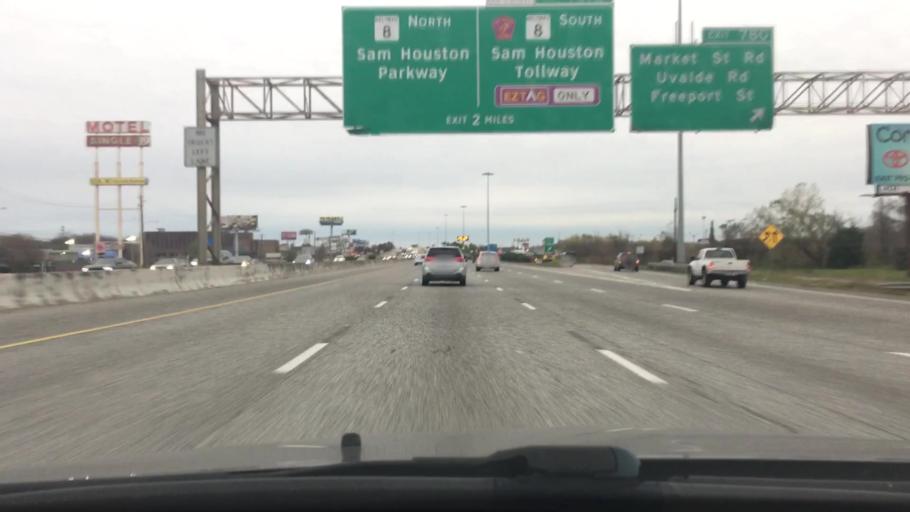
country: US
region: Texas
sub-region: Harris County
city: Cloverleaf
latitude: 29.7711
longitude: -95.1942
